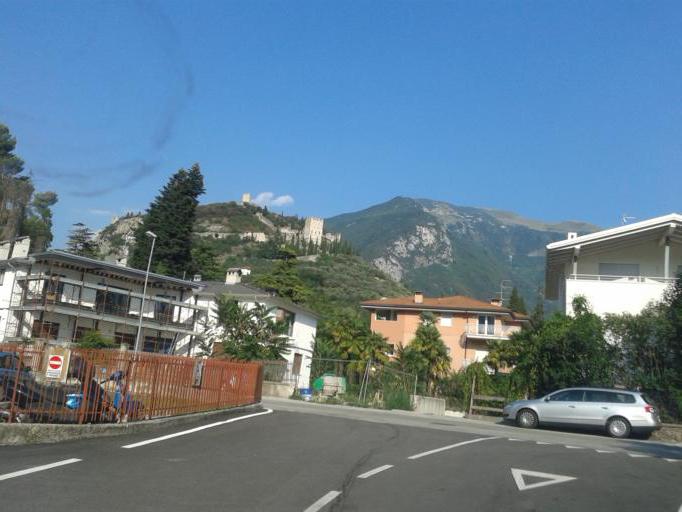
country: IT
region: Trentino-Alto Adige
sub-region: Provincia di Trento
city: Arco
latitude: 45.9202
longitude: 10.8802
